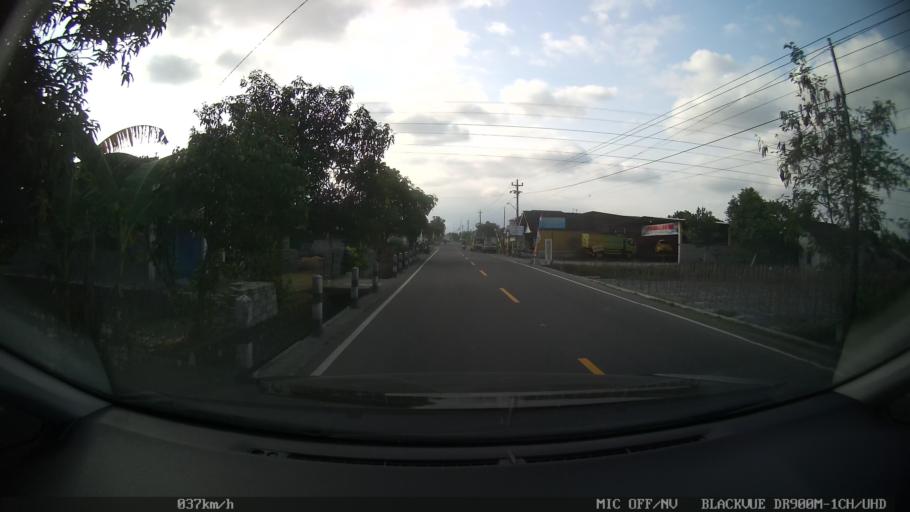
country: ID
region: Central Java
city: Candi Prambanan
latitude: -7.7143
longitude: 110.4712
